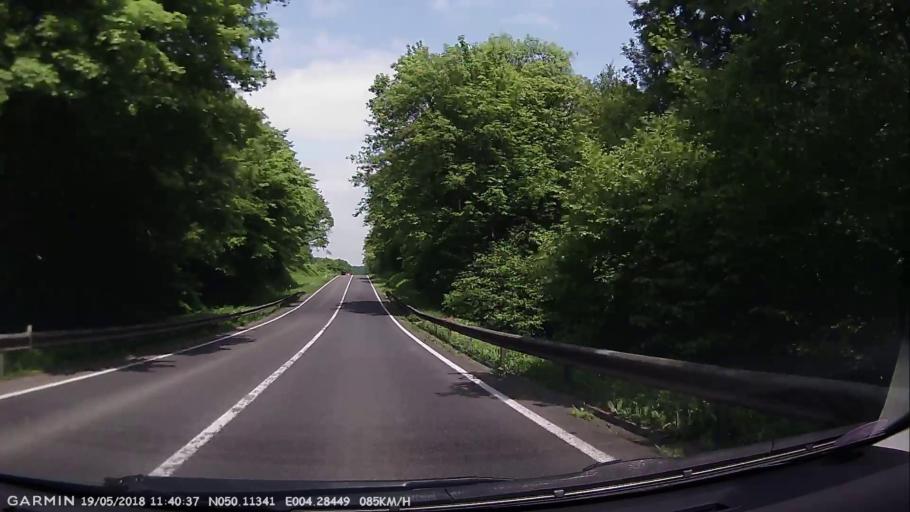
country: BE
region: Wallonia
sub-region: Province du Hainaut
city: Froidchapelle
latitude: 50.1136
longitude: 4.2844
